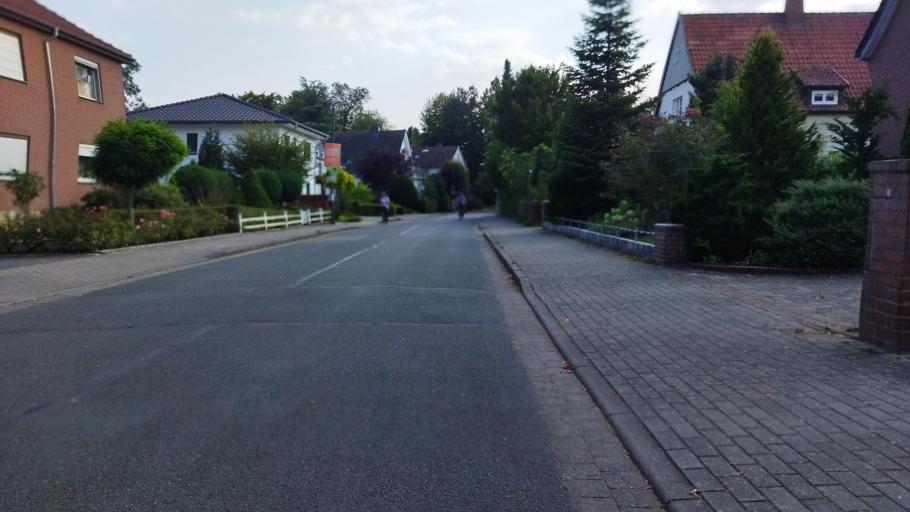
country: DE
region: Lower Saxony
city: Osnabrueck
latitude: 52.2423
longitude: 8.0260
